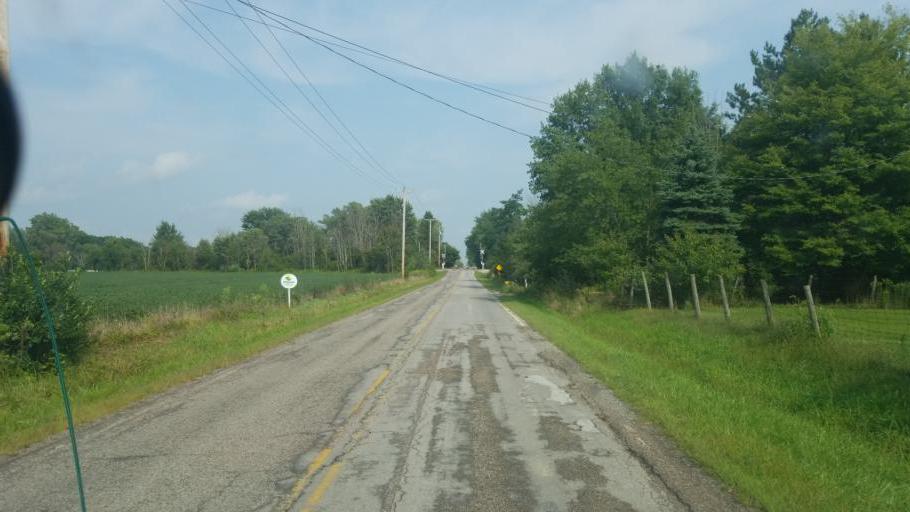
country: US
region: Ohio
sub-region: Medina County
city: Lodi
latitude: 41.1363
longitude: -82.0528
